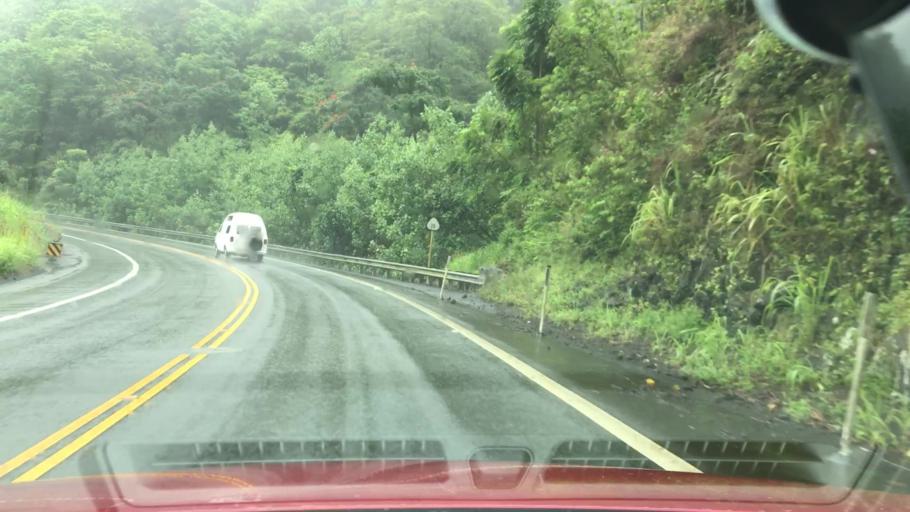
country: US
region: Hawaii
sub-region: Hawaii County
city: Pepeekeo
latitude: 19.9864
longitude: -155.2480
